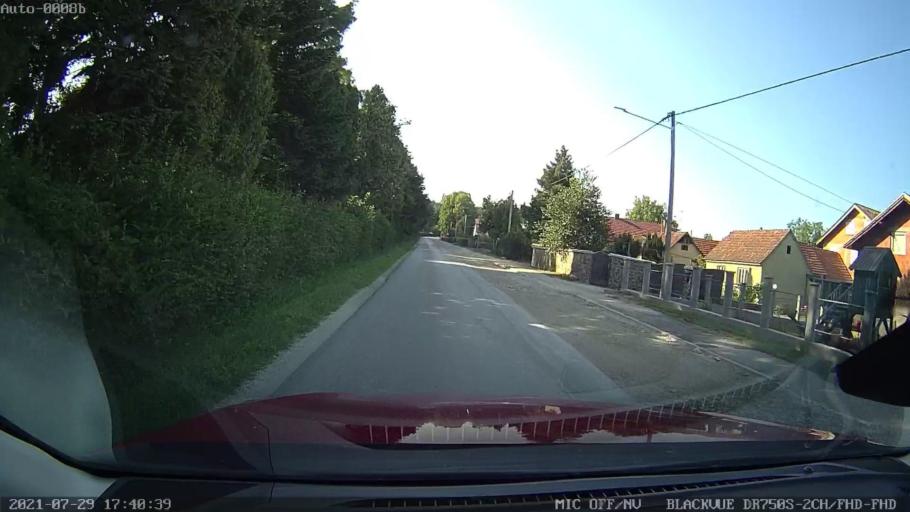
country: HR
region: Varazdinska
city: Vinica
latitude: 46.3237
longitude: 16.1533
